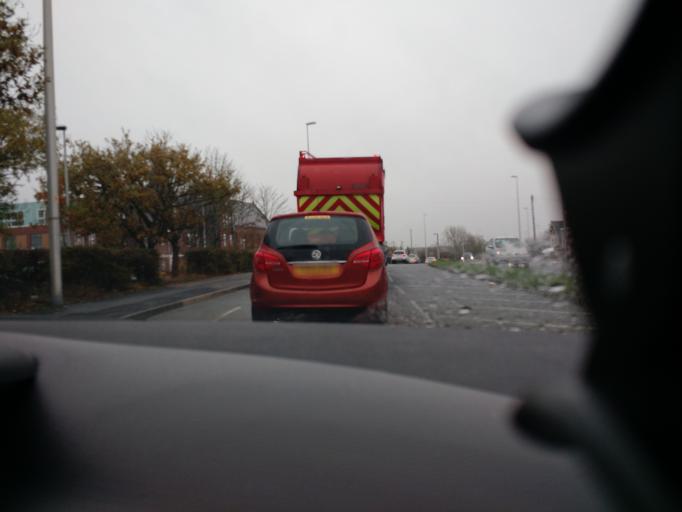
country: GB
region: England
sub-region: Lancashire
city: Great Marton
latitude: 53.8273
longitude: -3.0228
